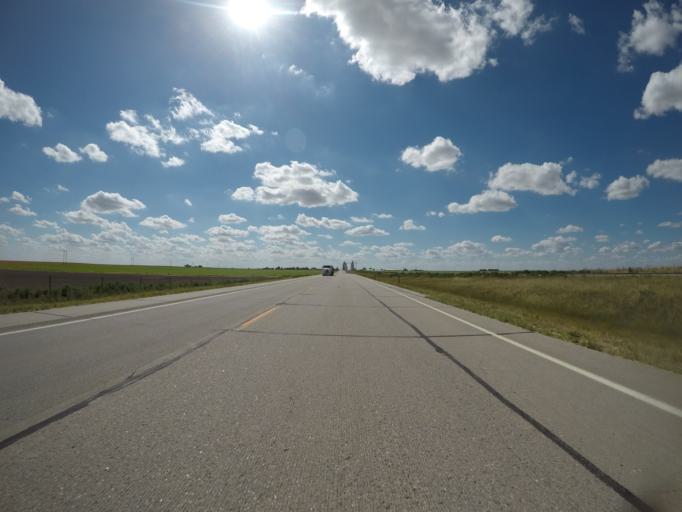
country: US
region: Colorado
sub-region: Phillips County
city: Holyoke
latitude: 40.6097
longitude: -102.4544
